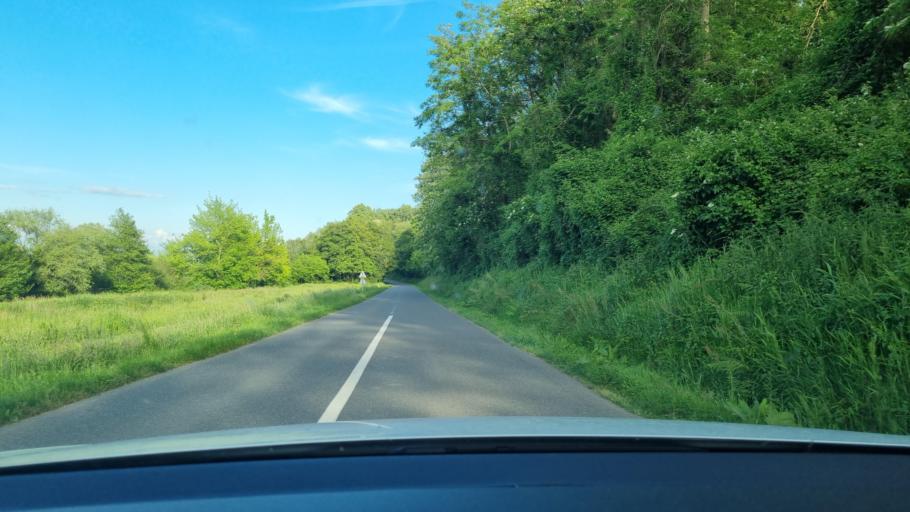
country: FR
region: Aquitaine
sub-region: Departement des Landes
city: Peyrehorade
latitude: 43.5372
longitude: -1.1586
